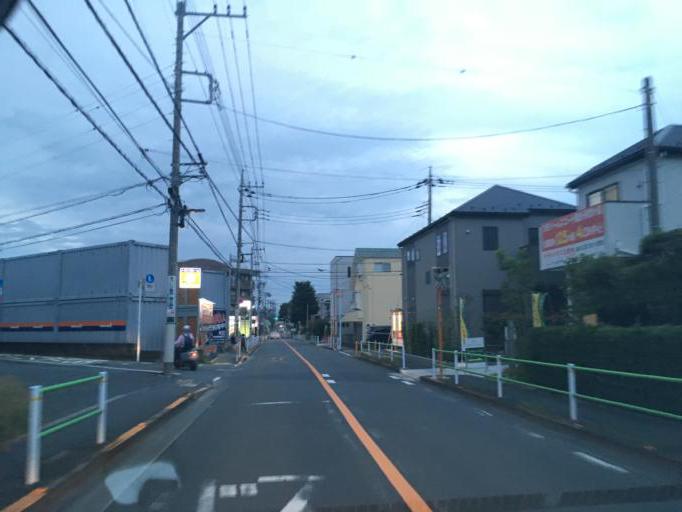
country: JP
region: Tokyo
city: Kokubunji
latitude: 35.7129
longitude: 139.4553
